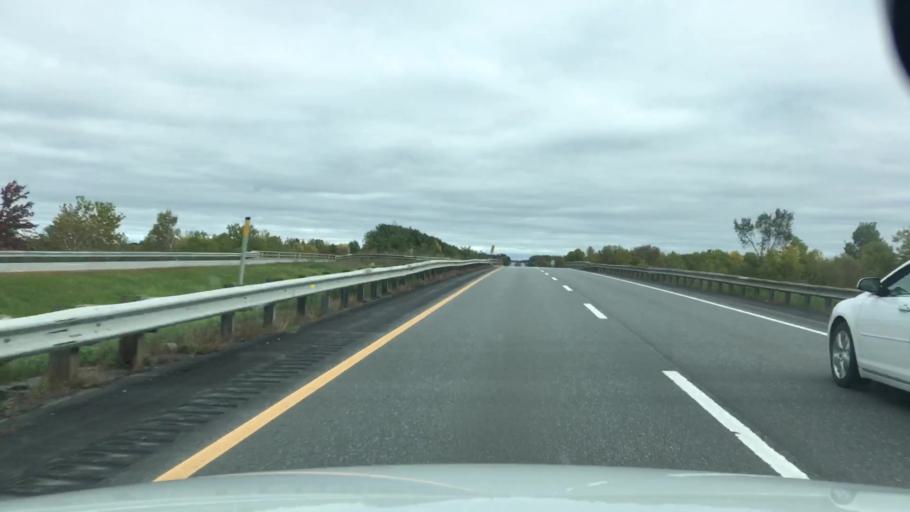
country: US
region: Maine
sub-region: Penobscot County
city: Newport
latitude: 44.8299
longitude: -69.2836
